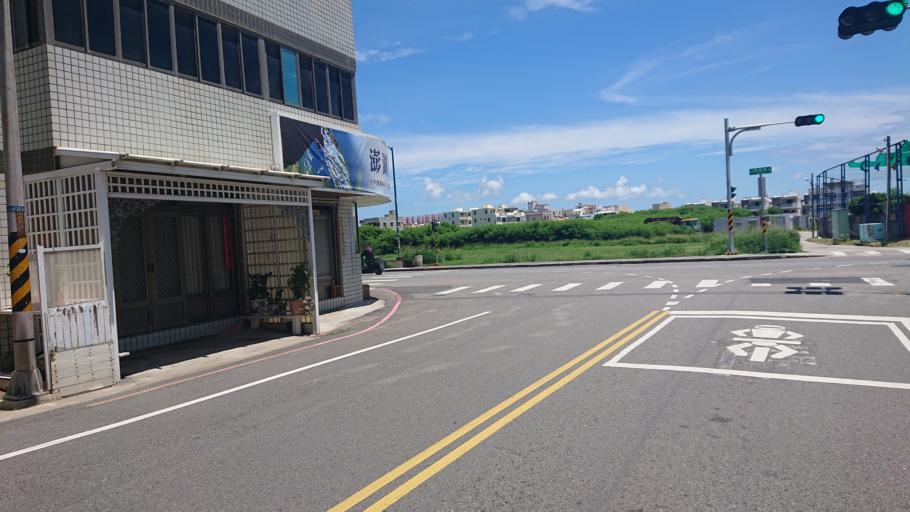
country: TW
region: Taiwan
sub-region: Penghu
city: Ma-kung
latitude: 23.5758
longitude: 119.5781
